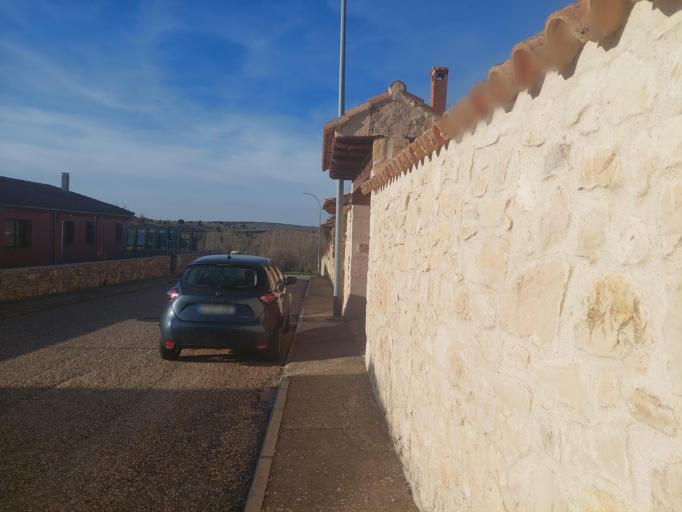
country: ES
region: Castille and Leon
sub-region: Provincia de Segovia
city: Pradena
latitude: 41.1354
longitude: -3.6931
